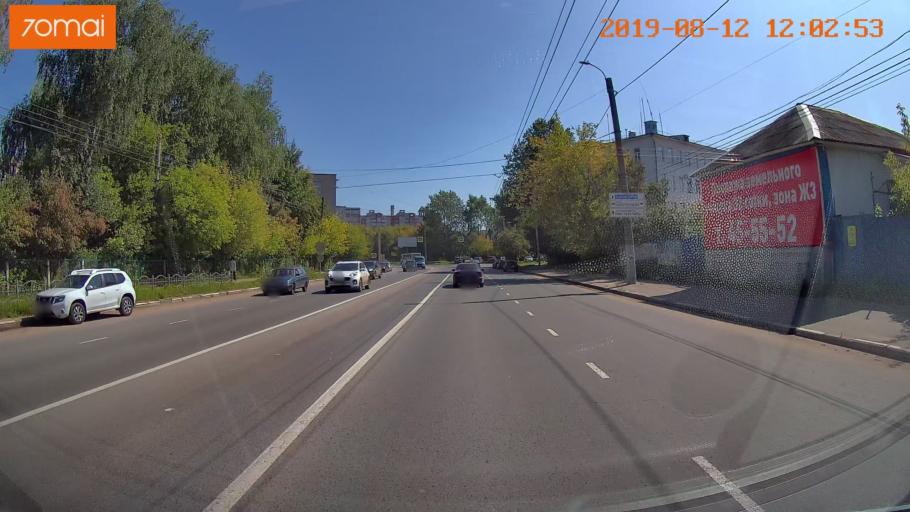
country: RU
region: Ivanovo
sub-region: Gorod Ivanovo
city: Ivanovo
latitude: 56.9953
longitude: 40.9951
